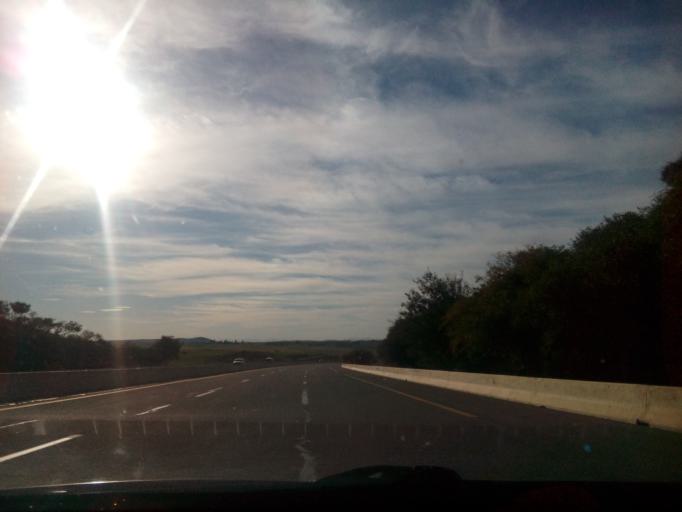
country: DZ
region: Tlemcen
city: Beni Mester
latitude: 34.9040
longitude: -1.5704
